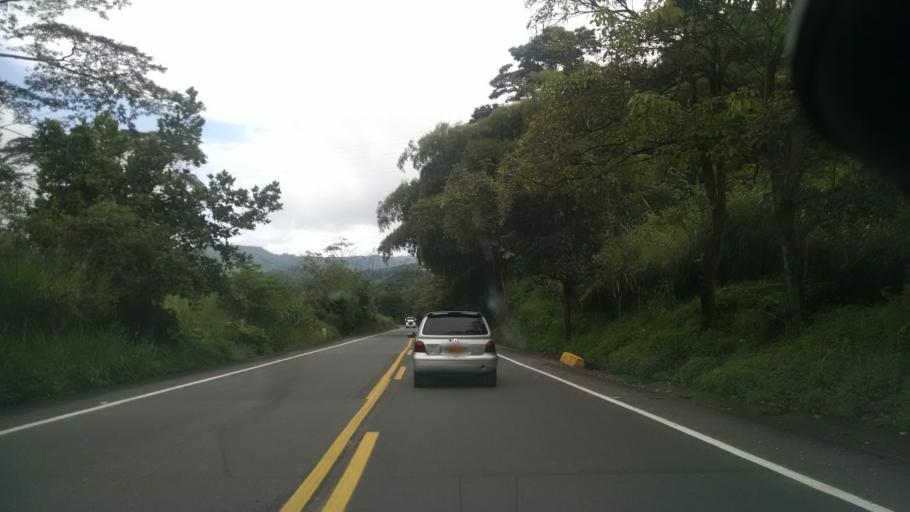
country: CO
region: Caldas
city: Palestina
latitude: 5.0318
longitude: -75.5981
